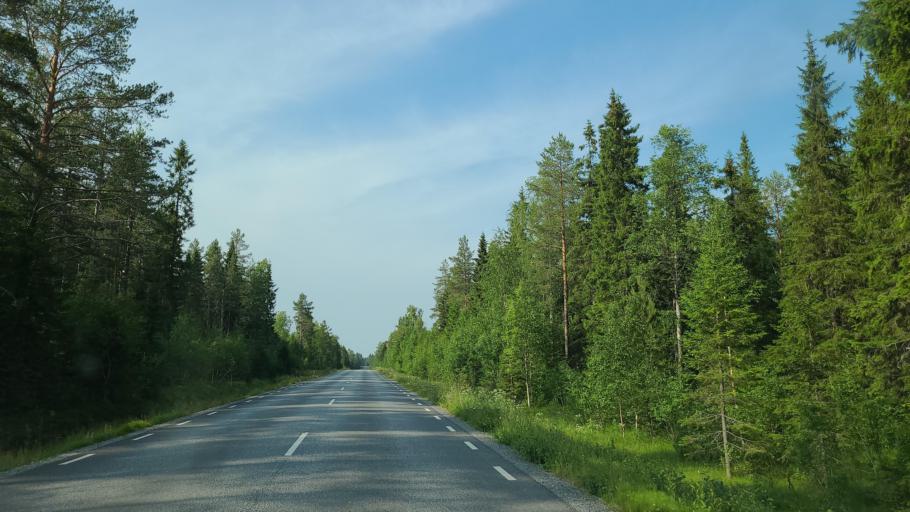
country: SE
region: Vaesterbotten
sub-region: Skelleftea Kommun
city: Burea
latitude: 64.4327
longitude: 21.3539
